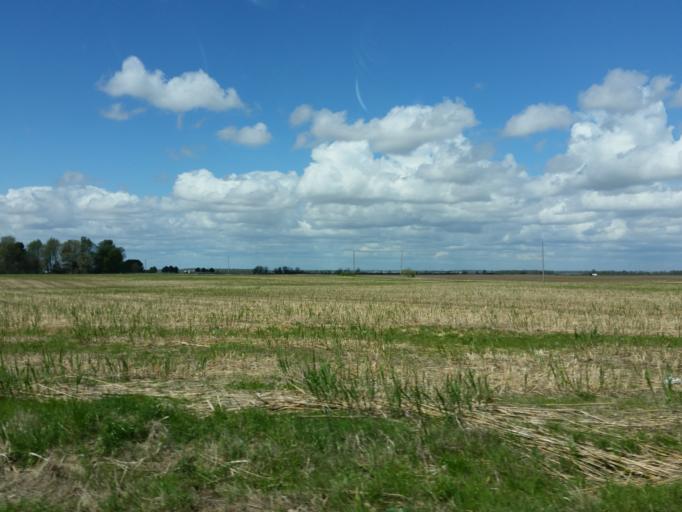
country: US
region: Arkansas
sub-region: Craighead County
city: Bono
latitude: 36.0165
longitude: -90.6951
